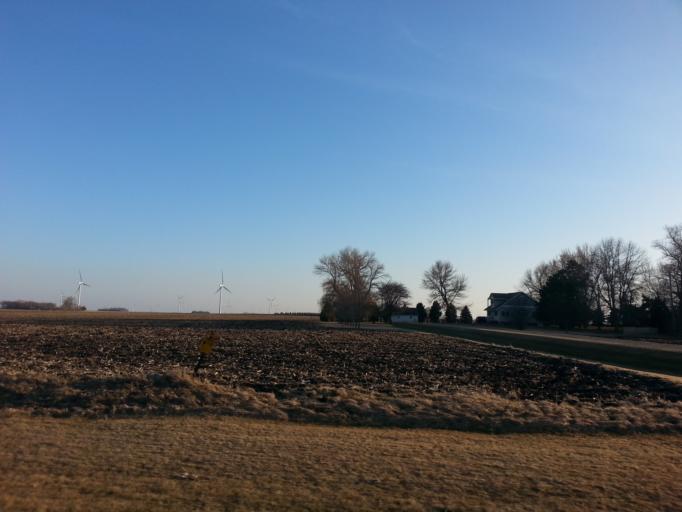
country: US
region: Iowa
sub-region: Worth County
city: Northwood
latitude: 43.4359
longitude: -93.0899
